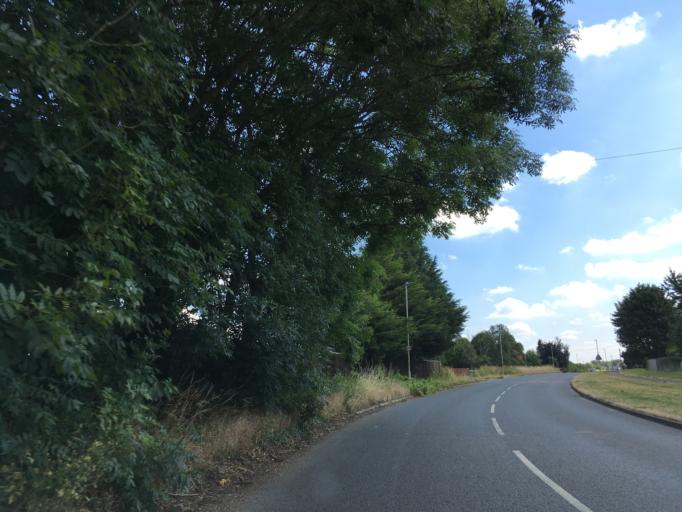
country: GB
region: England
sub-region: Gloucestershire
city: Barnwood
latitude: 51.8884
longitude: -2.2130
